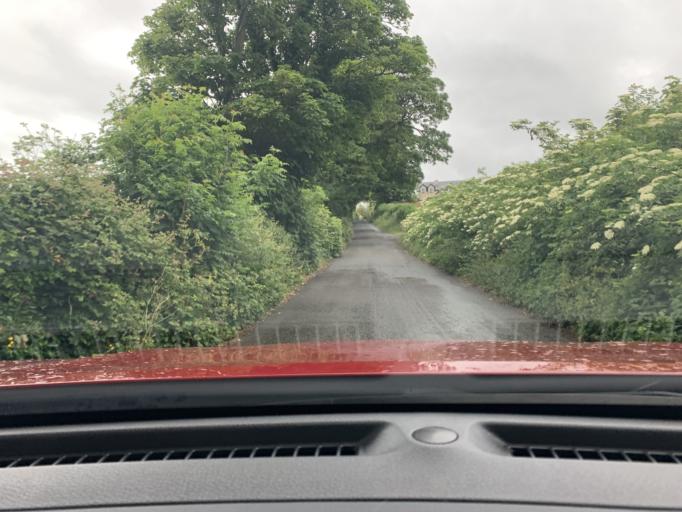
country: IE
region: Connaught
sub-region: Sligo
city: Sligo
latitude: 54.2921
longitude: -8.4635
